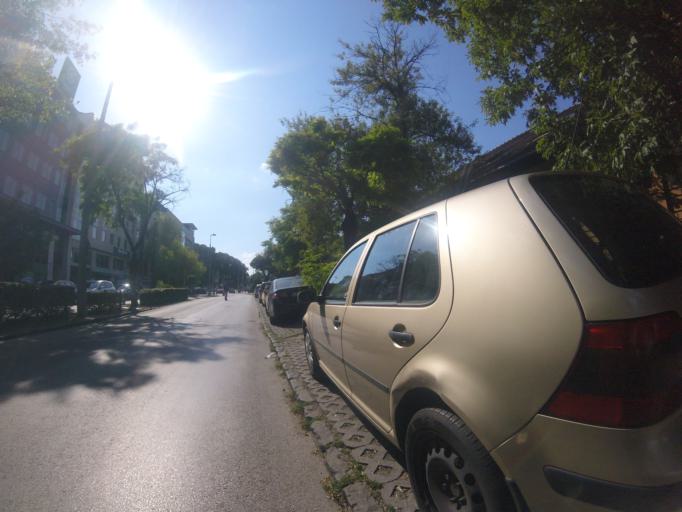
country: HU
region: Budapest
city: Budapest XIII. keruelet
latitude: 47.5481
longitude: 19.0751
